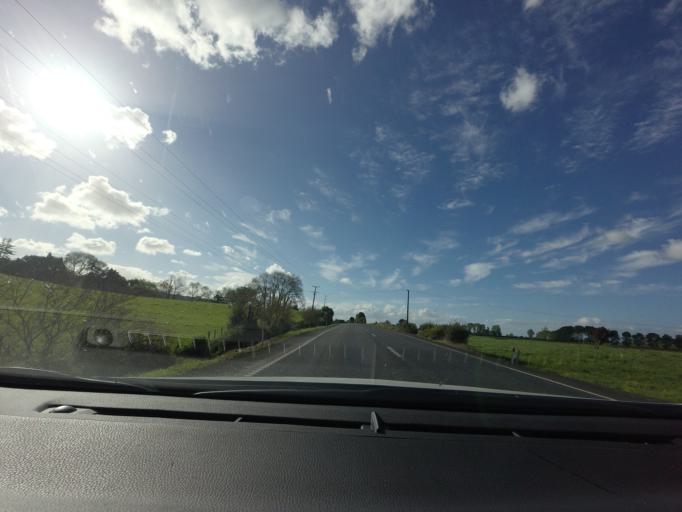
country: NZ
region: Waikato
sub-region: Hauraki District
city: Ngatea
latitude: -37.4407
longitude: 175.4996
